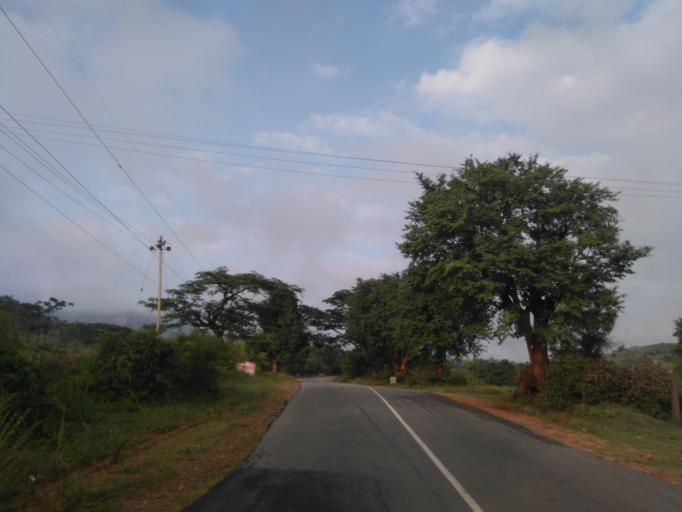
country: IN
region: Karnataka
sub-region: Ramanagara
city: Kanakapura
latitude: 12.4965
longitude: 77.3811
